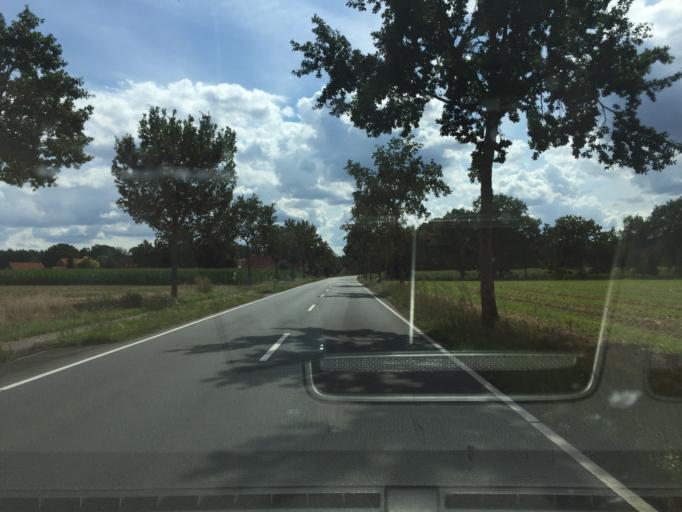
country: DE
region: Lower Saxony
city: Rethem
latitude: 52.7577
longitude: 9.3516
